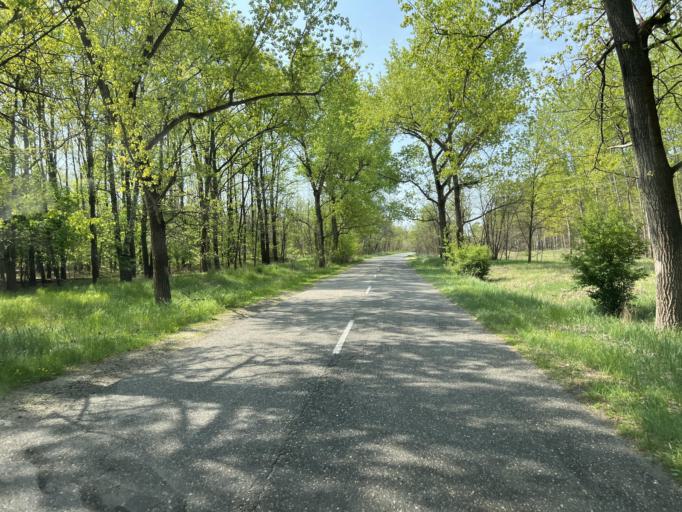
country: HU
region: Pest
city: Tortel
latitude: 47.0797
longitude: 19.8725
